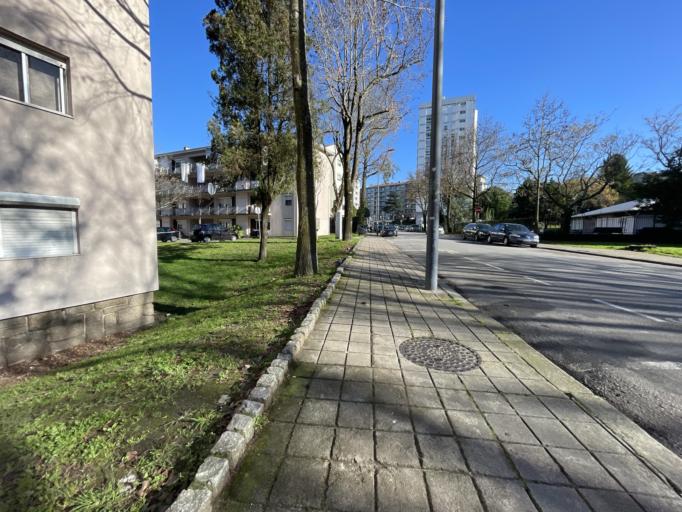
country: PT
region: Porto
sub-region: Porto
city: Porto
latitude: 41.1536
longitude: -8.5982
